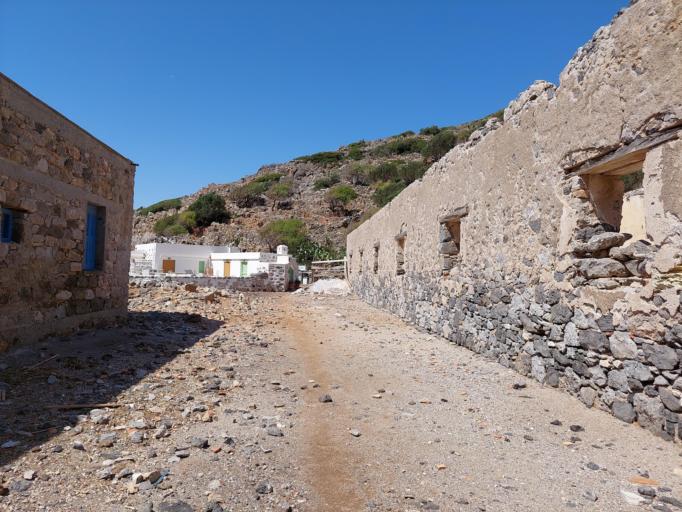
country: GR
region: South Aegean
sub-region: Nomos Dodekanisou
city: Karpathos
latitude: 35.8224
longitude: 27.2222
